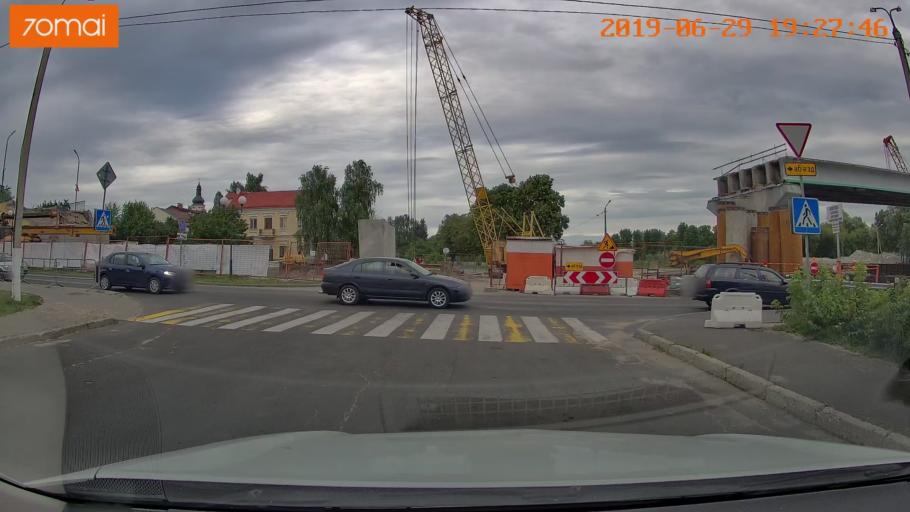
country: BY
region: Brest
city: Pinsk
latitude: 52.1107
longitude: 26.1046
